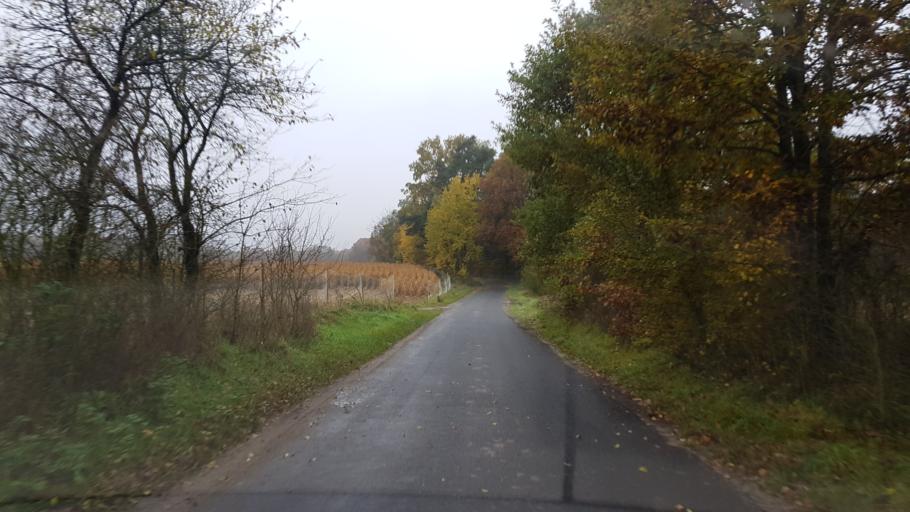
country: PL
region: West Pomeranian Voivodeship
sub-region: Powiat gryfinski
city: Chojna
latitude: 53.0468
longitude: 14.4784
